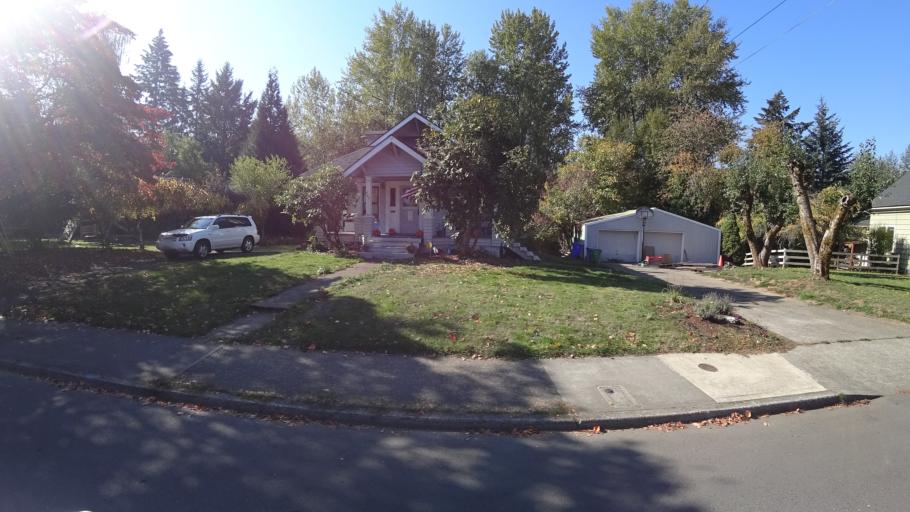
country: US
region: Oregon
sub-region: Multnomah County
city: Gresham
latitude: 45.4924
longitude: -122.4257
